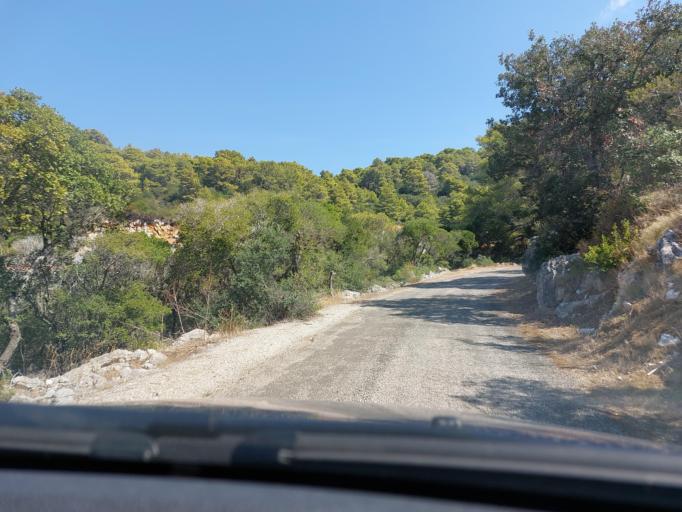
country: HR
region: Dubrovacko-Neretvanska
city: Smokvica
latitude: 42.7716
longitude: 16.8378
